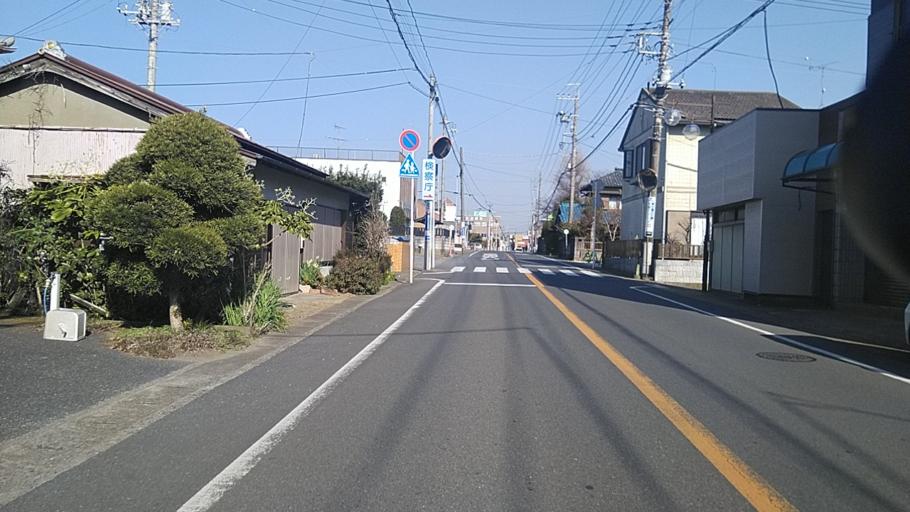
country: JP
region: Chiba
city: Yokaichiba
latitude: 35.6986
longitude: 140.5426
